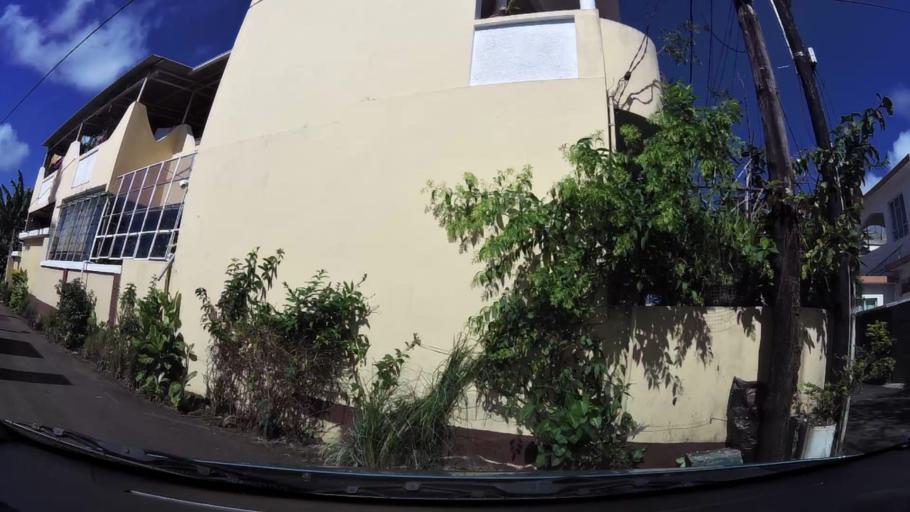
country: MU
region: Grand Port
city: Plaine Magnien
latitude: -20.4274
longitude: 57.6693
